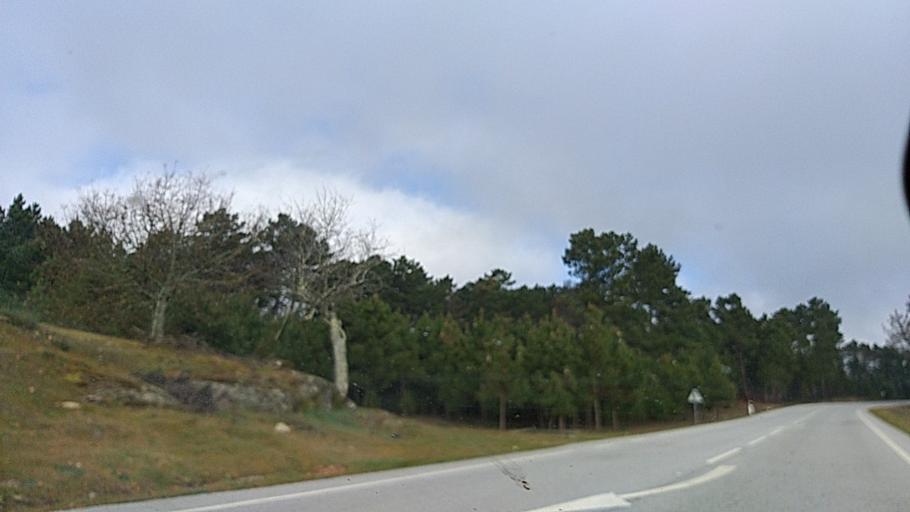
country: PT
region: Guarda
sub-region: Aguiar da Beira
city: Aguiar da Beira
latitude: 40.7490
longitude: -7.5044
